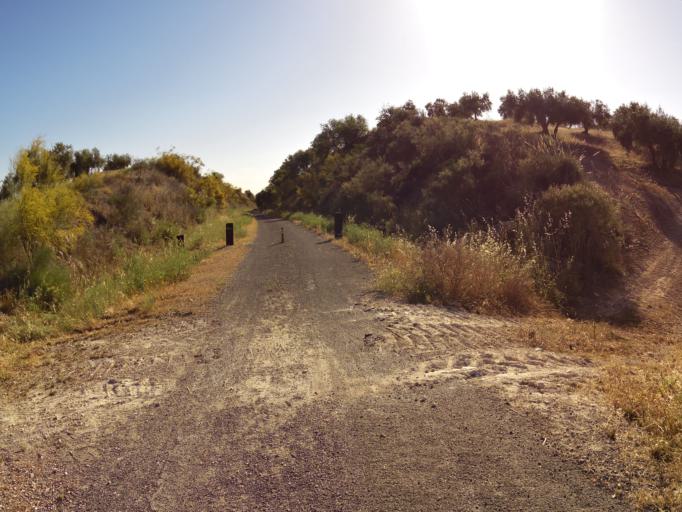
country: ES
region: Andalusia
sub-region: Province of Cordoba
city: Luque
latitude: 37.5650
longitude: -4.2405
